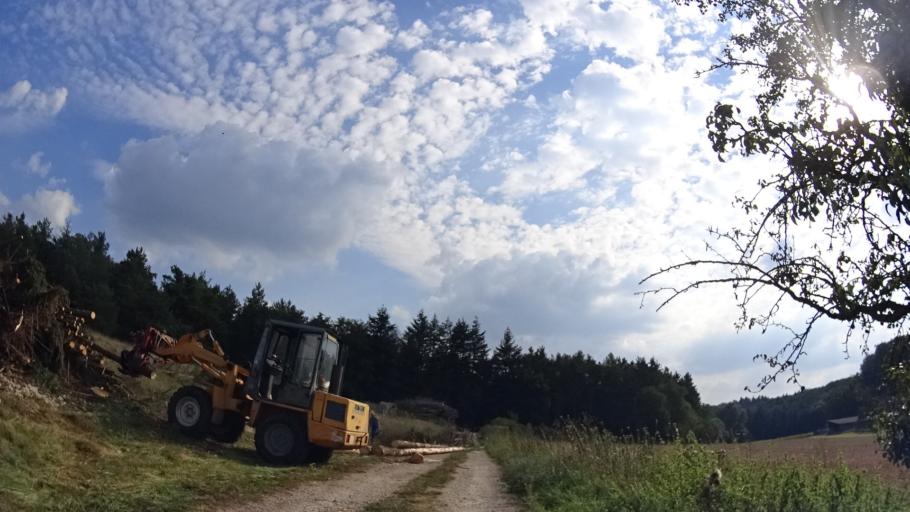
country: DE
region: Bavaria
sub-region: Lower Bavaria
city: Riedenburg
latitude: 48.9532
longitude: 11.6606
